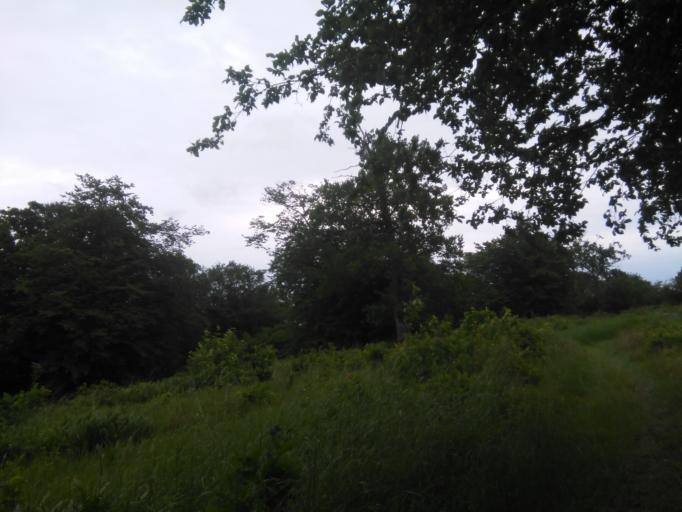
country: DK
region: Capital Region
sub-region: Bornholm Kommune
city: Akirkeby
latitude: 55.1144
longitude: 14.9068
